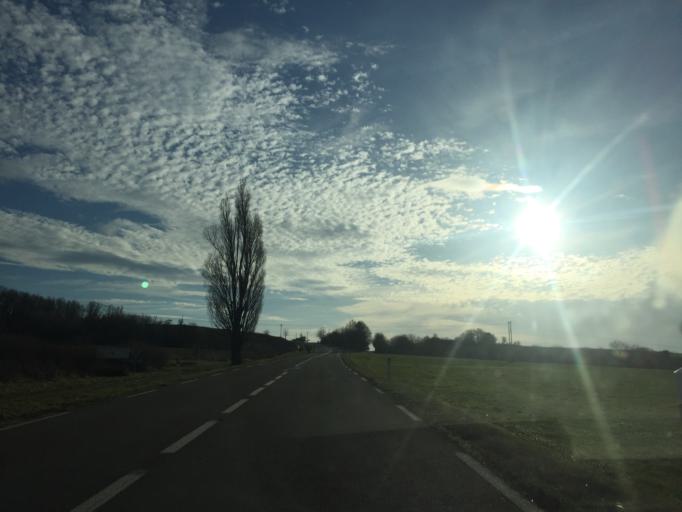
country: FR
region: Franche-Comte
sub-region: Departement du Jura
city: Arbois
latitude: 46.9366
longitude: 5.7773
